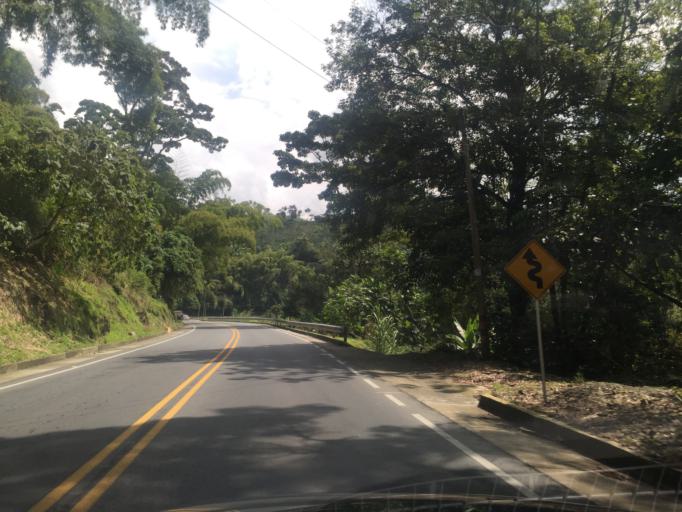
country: CO
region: Caldas
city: Chinchina
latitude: 4.9881
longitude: -75.5917
